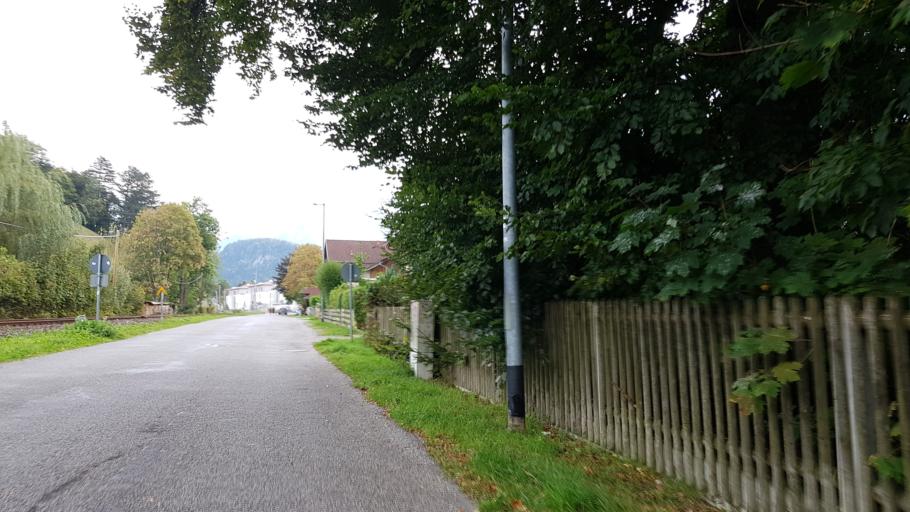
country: DE
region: Bavaria
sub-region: Swabia
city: Fuessen
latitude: 47.5728
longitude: 10.6905
